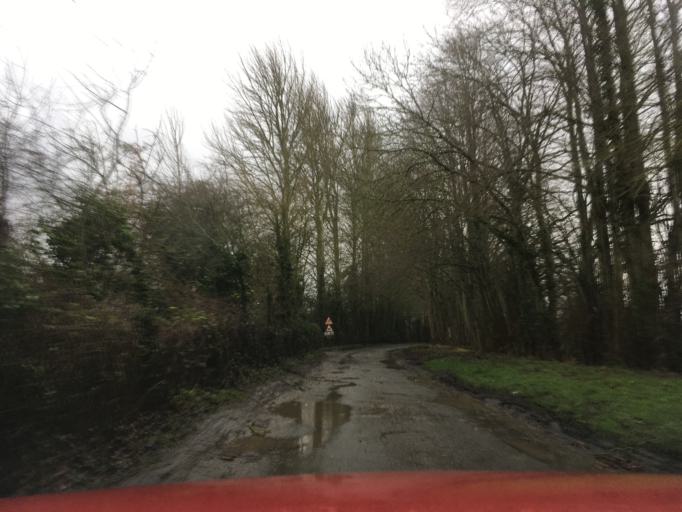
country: GB
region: England
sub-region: Oxfordshire
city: Oxford
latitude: 51.7628
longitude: -1.2865
